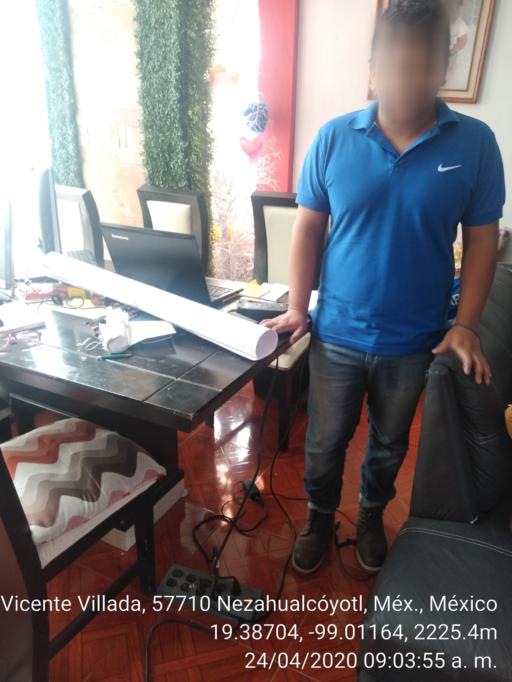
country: MX
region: Mexico
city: Ciudad Nezahualcoyotl
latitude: 19.3870
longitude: -99.0116
